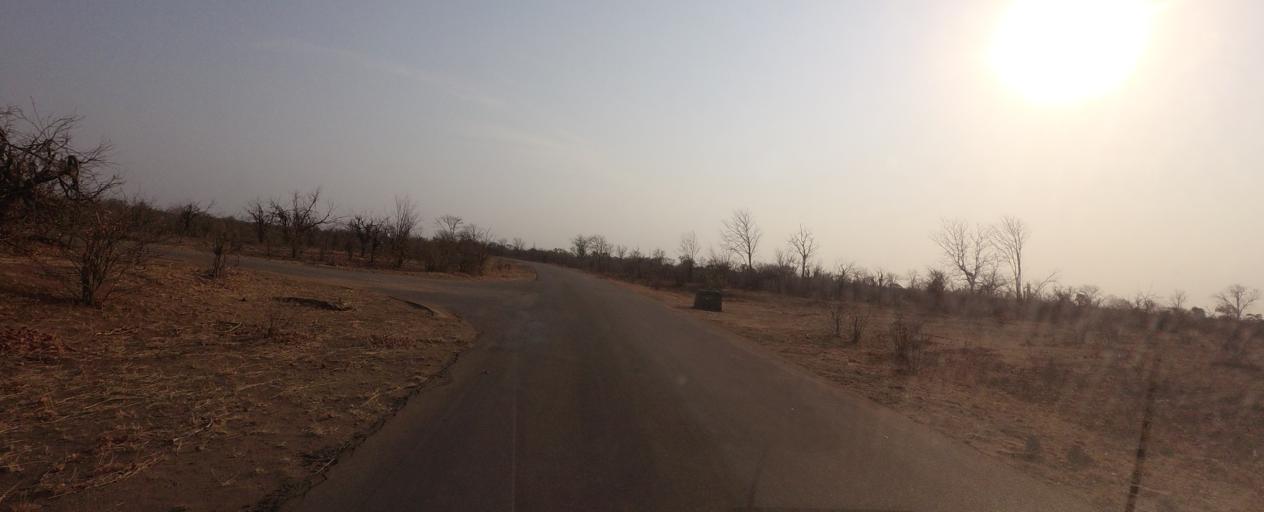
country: ZA
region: Limpopo
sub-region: Mopani District Municipality
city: Giyani
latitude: -23.0923
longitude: 31.4201
